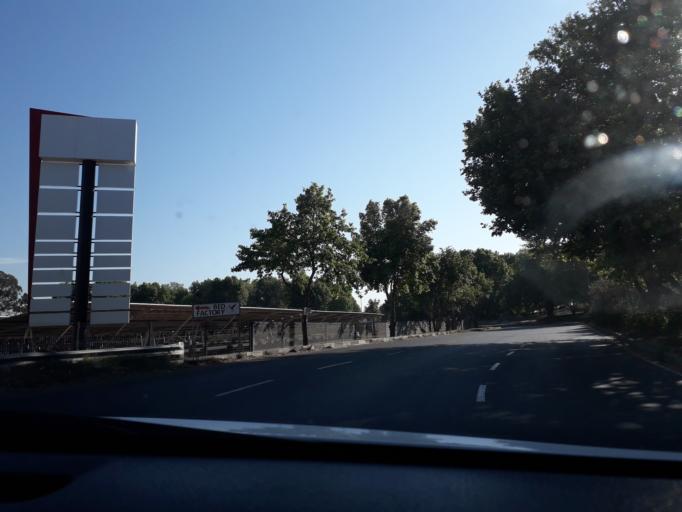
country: ZA
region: Gauteng
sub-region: City of Johannesburg Metropolitan Municipality
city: Modderfontein
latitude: -26.1088
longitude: 28.2377
